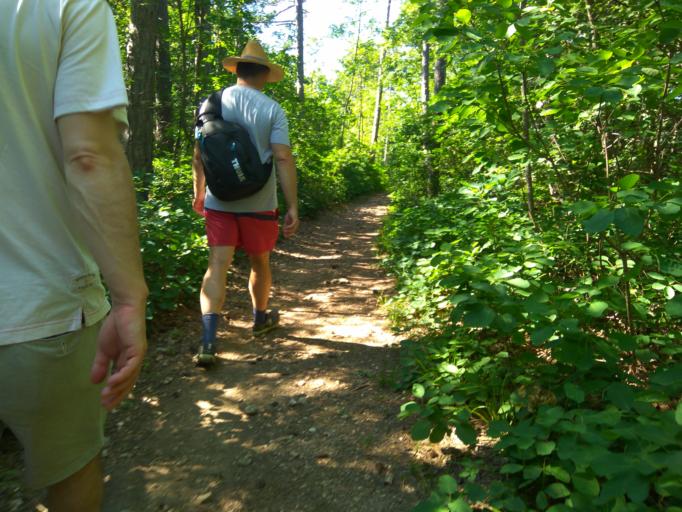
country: HU
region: Veszprem
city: Balatonfured
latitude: 46.9864
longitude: 17.8791
